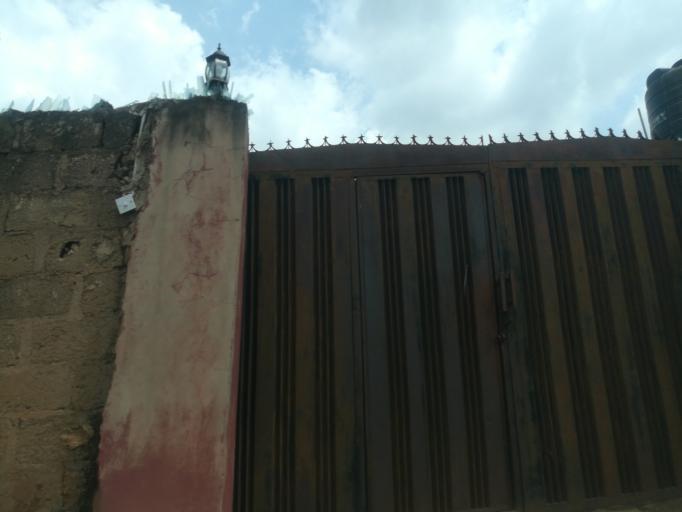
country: NG
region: Oyo
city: Ibadan
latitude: 7.4331
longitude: 3.9351
